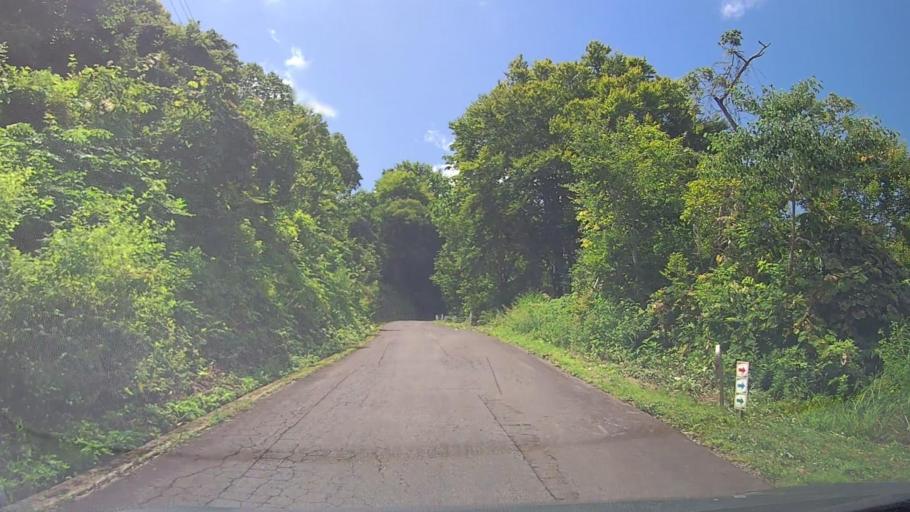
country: JP
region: Nagano
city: Iiyama
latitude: 36.9310
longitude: 138.4699
